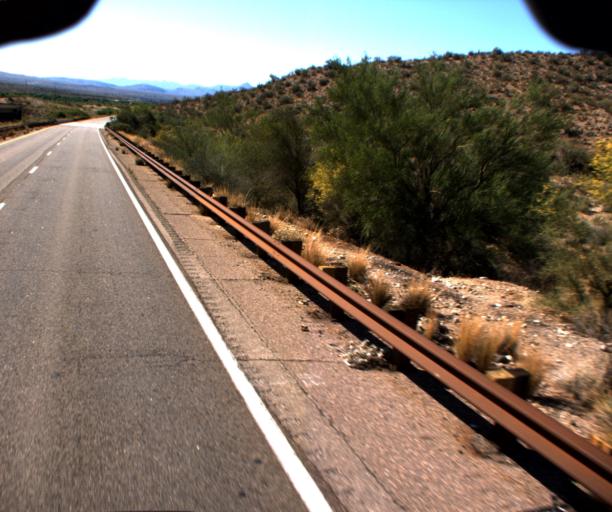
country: US
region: Arizona
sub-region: Yavapai County
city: Bagdad
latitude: 34.6776
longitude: -113.5928
